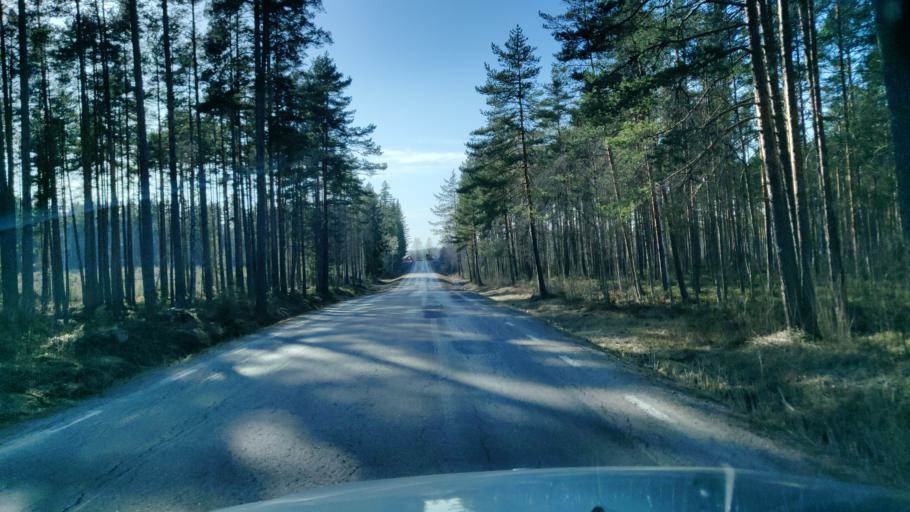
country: SE
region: Vaermland
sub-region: Sunne Kommun
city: Sunne
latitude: 59.9928
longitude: 13.3018
